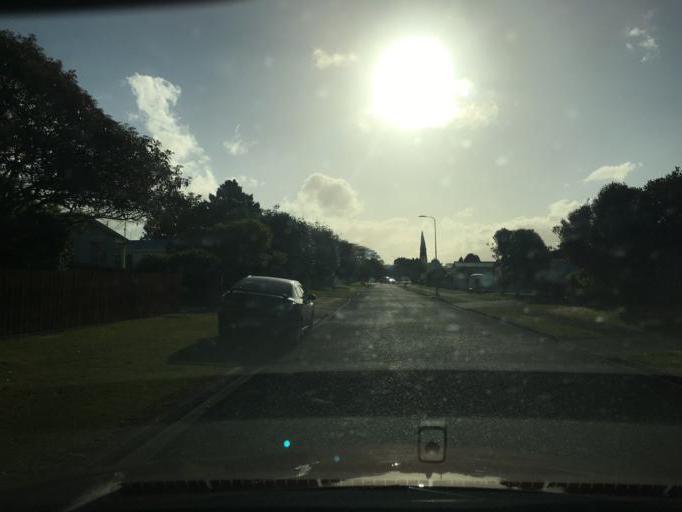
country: NZ
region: Waikato
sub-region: Waipa District
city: Cambridge
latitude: -38.0048
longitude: 175.3385
